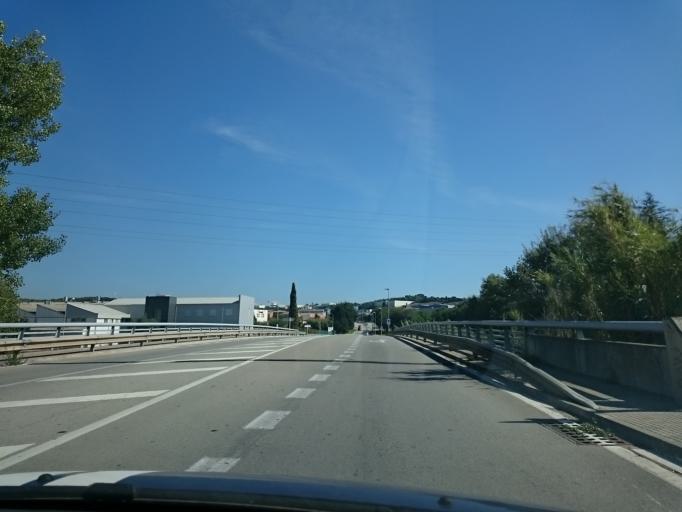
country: ES
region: Catalonia
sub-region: Provincia de Barcelona
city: Llica de Vall
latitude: 41.5864
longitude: 2.2451
